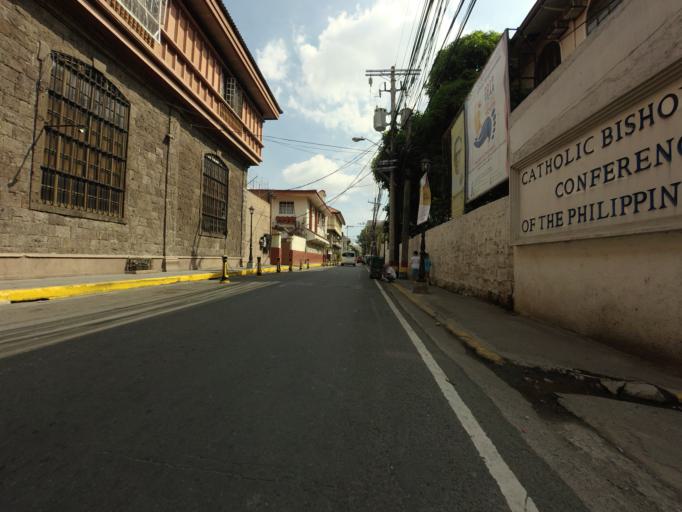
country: PH
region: Metro Manila
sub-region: City of Manila
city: Port Area
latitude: 14.5900
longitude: 120.9746
